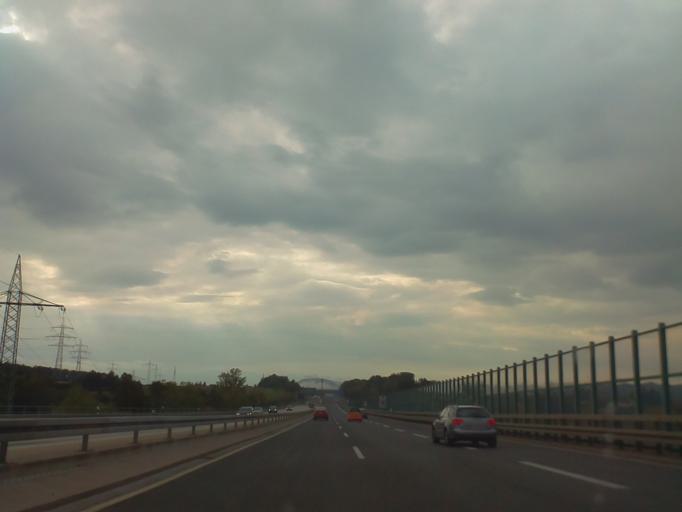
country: DE
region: Hesse
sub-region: Regierungsbezirk Kassel
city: Eichenzell
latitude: 50.4901
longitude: 9.7015
